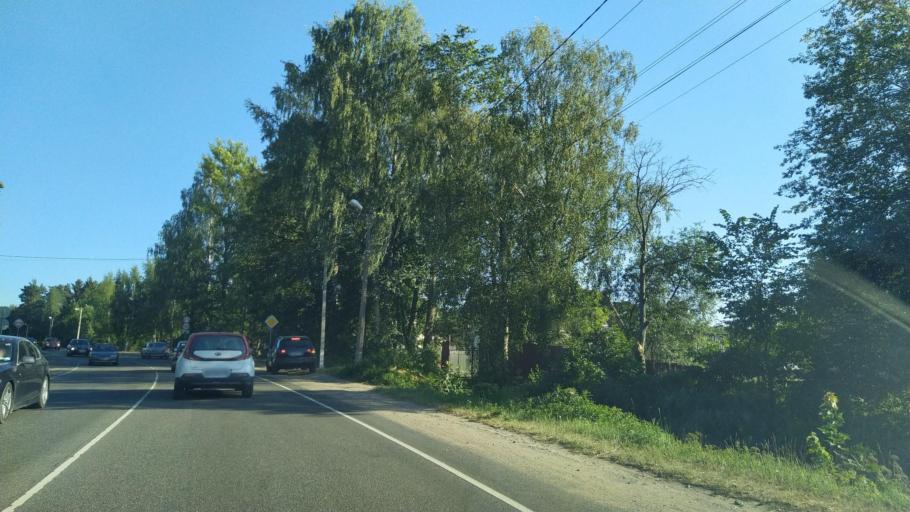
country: RU
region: Leningrad
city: Toksovo
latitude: 60.1471
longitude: 30.5235
